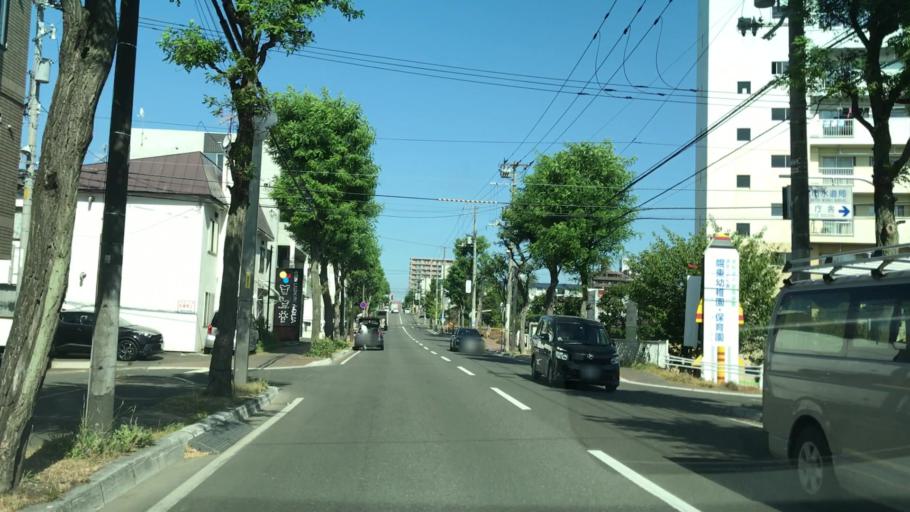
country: JP
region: Hokkaido
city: Sapporo
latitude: 43.0466
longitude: 141.4061
